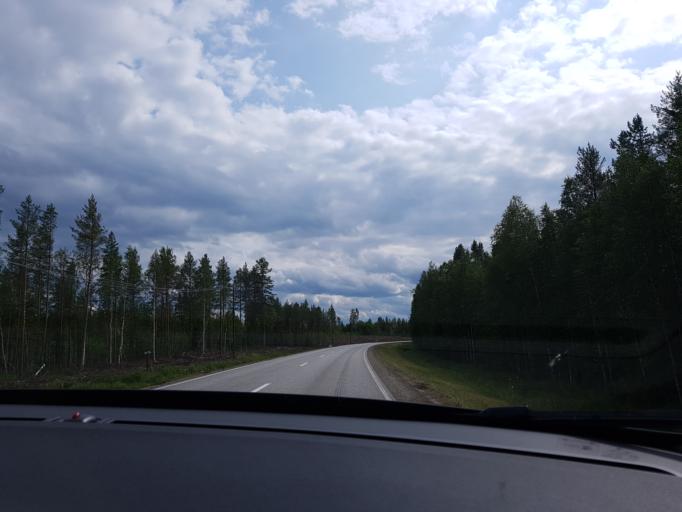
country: FI
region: Kainuu
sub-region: Kehys-Kainuu
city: Kuhmo
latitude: 64.3653
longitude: 29.8931
